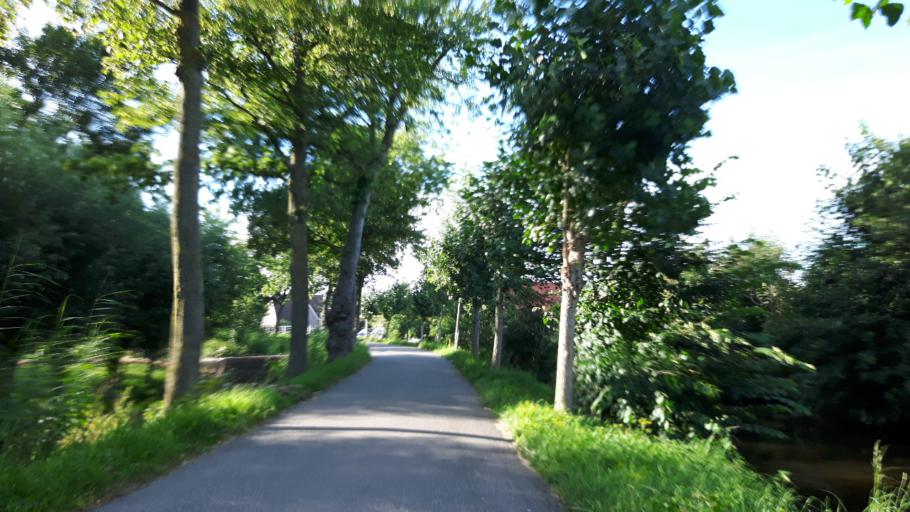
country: NL
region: Utrecht
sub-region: Gemeente Woerden
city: Woerden
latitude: 52.0723
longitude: 4.9016
